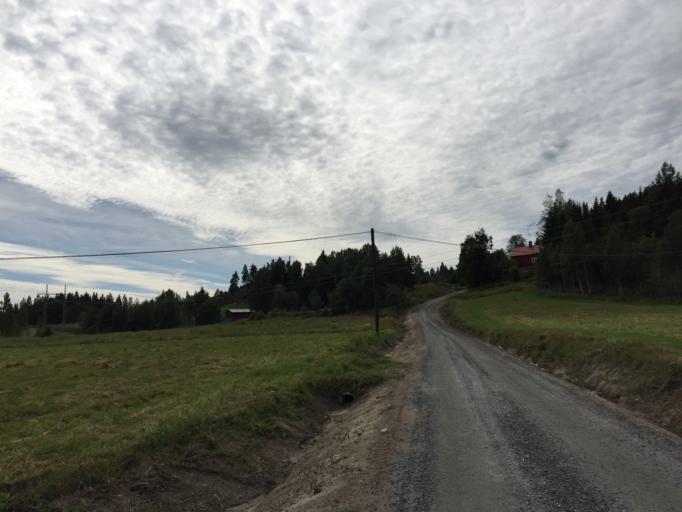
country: SE
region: Gaevleborg
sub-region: Ljusdals Kommun
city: Jaervsoe
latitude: 61.7369
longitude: 16.2779
